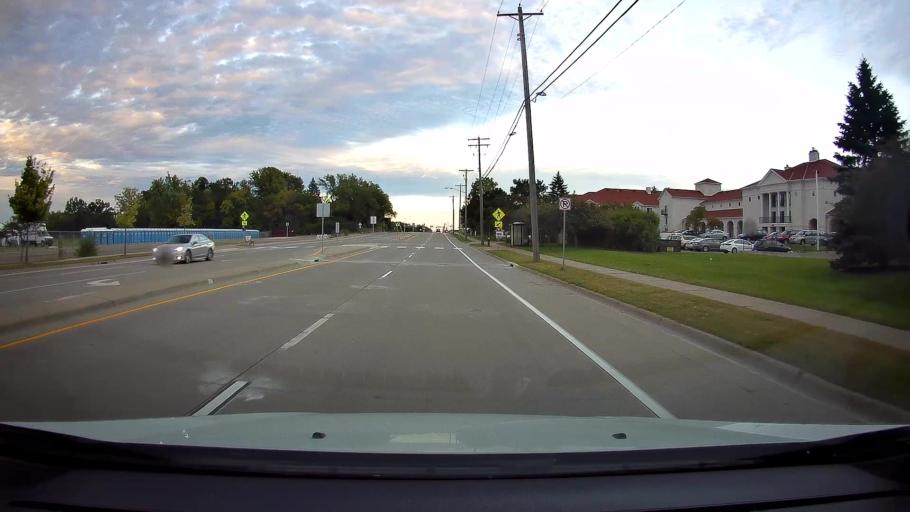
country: US
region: Minnesota
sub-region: Ramsey County
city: Lauderdale
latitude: 44.9916
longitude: -93.1920
